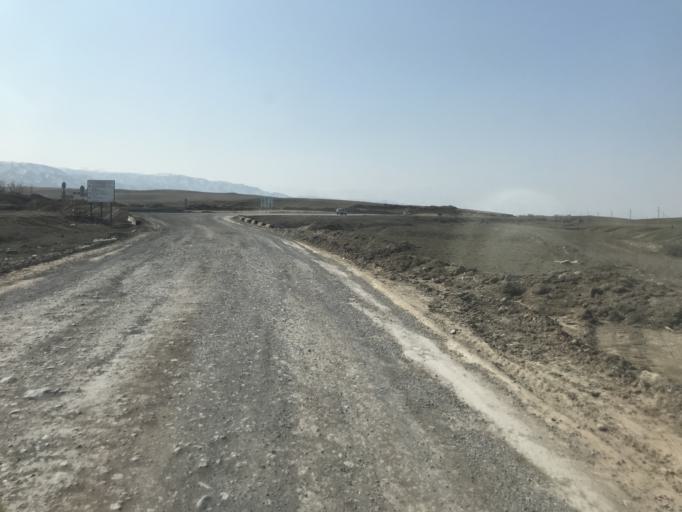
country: KG
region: Chuy
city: Bystrovka
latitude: 43.3197
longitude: 75.7984
